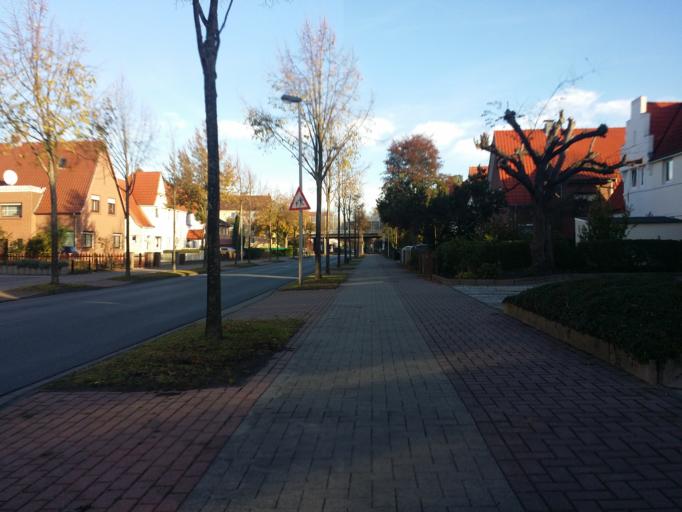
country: DE
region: Lower Saxony
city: Delmenhorst
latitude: 53.0308
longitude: 8.6393
